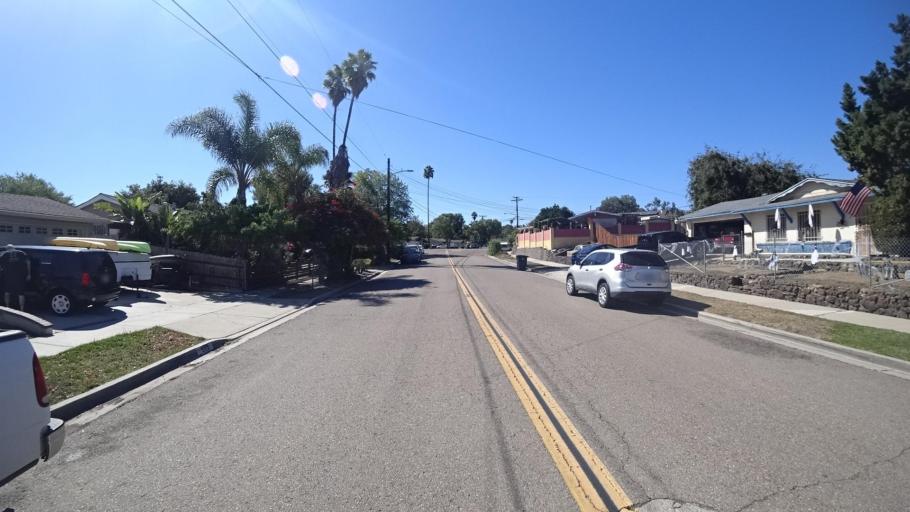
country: US
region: California
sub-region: San Diego County
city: La Presa
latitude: 32.7040
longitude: -117.0133
